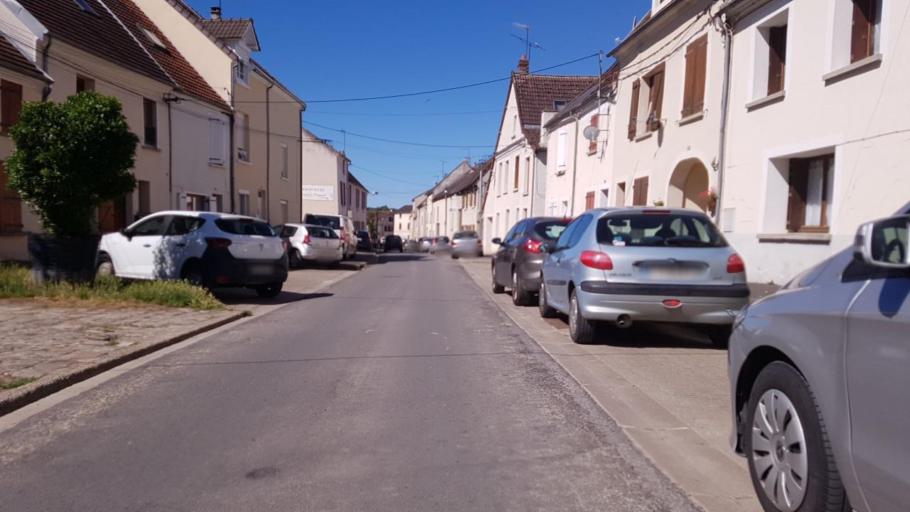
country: FR
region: Picardie
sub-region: Departement de l'Aisne
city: Charly-sur-Marne
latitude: 48.9791
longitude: 3.2860
